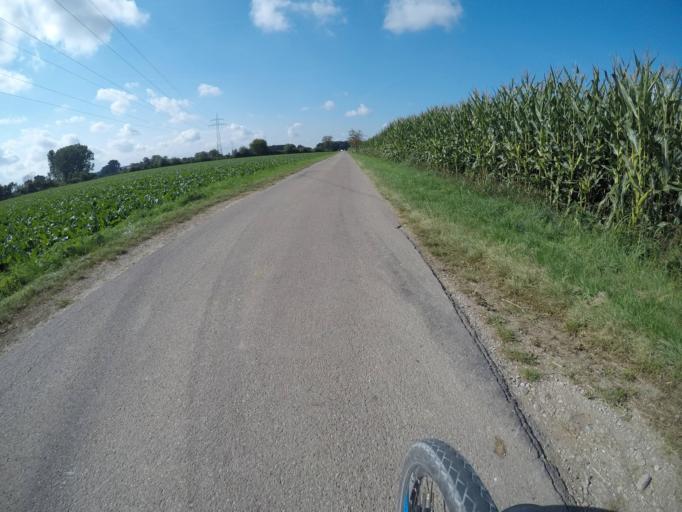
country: DE
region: Bavaria
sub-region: Swabia
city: Tapfheim
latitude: 48.6357
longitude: 10.6938
